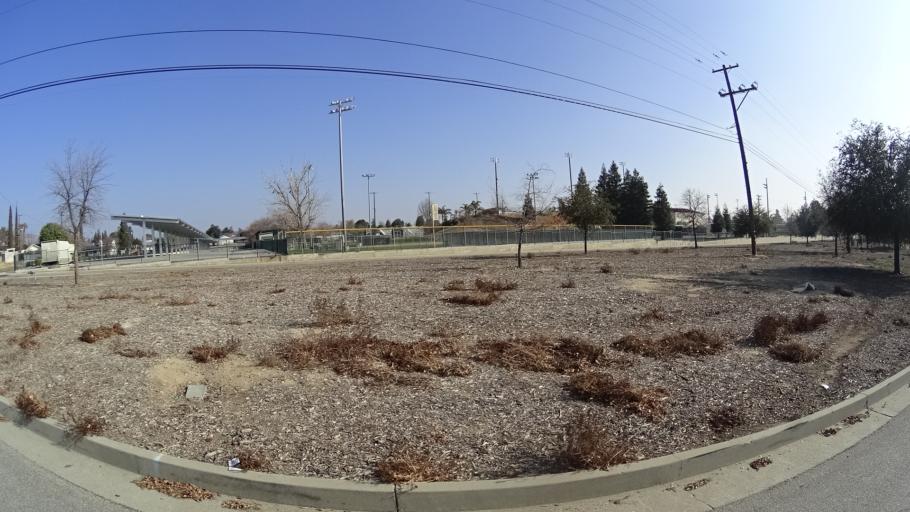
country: US
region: California
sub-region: Kern County
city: Oildale
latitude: 35.4008
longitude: -119.0032
